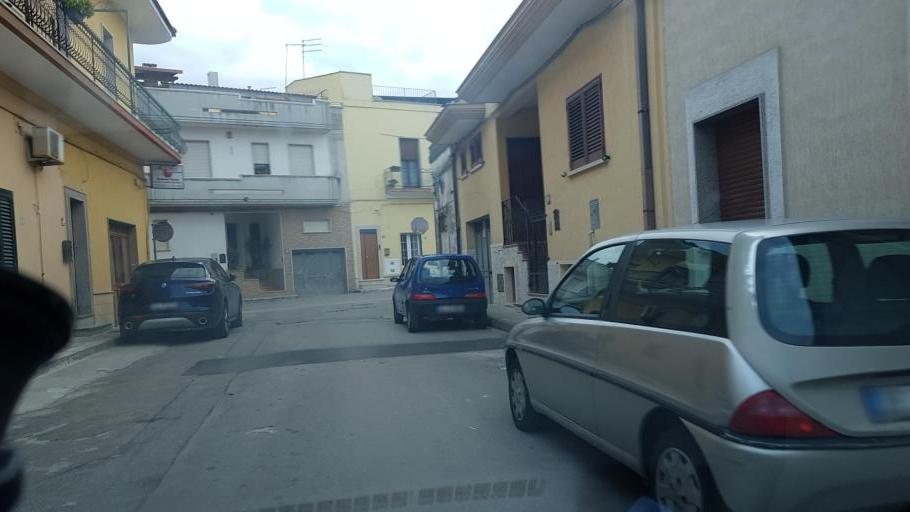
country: IT
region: Apulia
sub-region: Provincia di Brindisi
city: Oria
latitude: 40.5022
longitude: 17.6424
